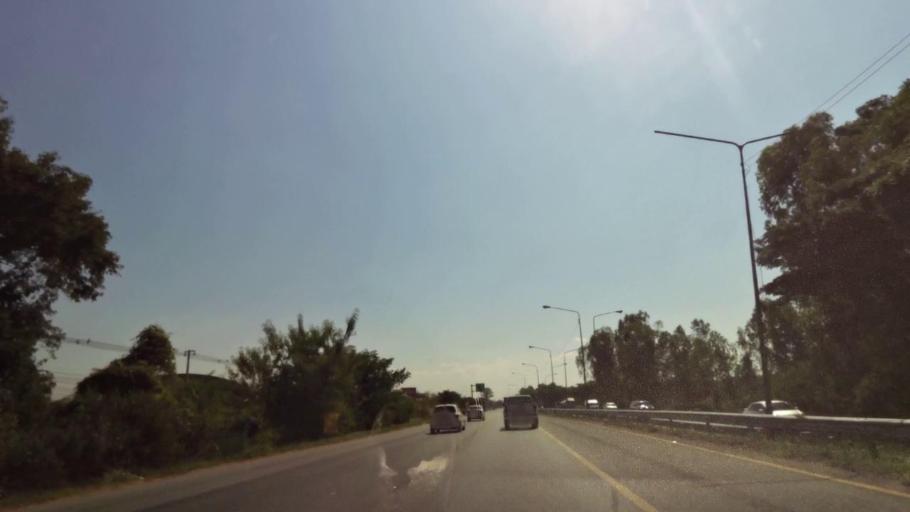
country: TH
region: Nakhon Sawan
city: Nakhon Sawan
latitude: 15.7811
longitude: 100.1211
